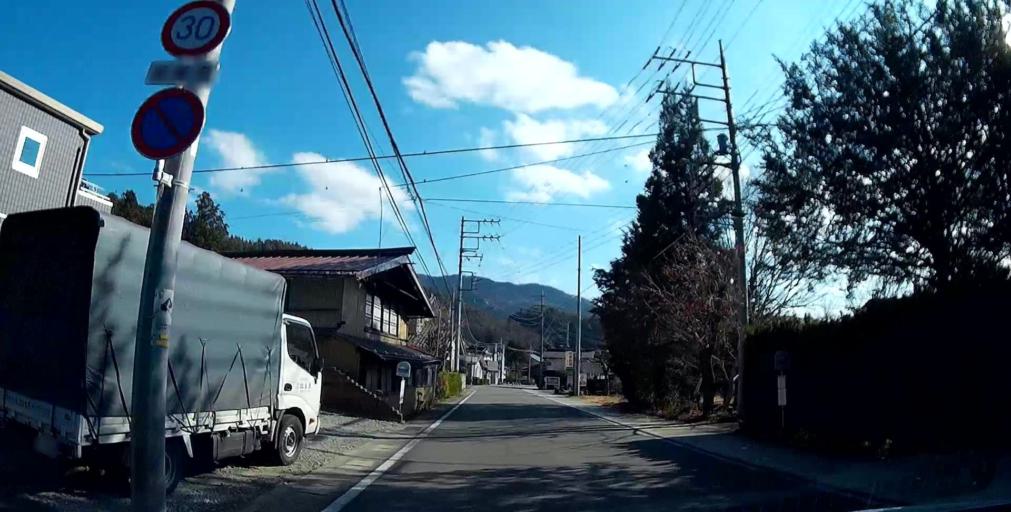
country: JP
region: Yamanashi
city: Fujikawaguchiko
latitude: 35.5313
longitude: 138.7724
